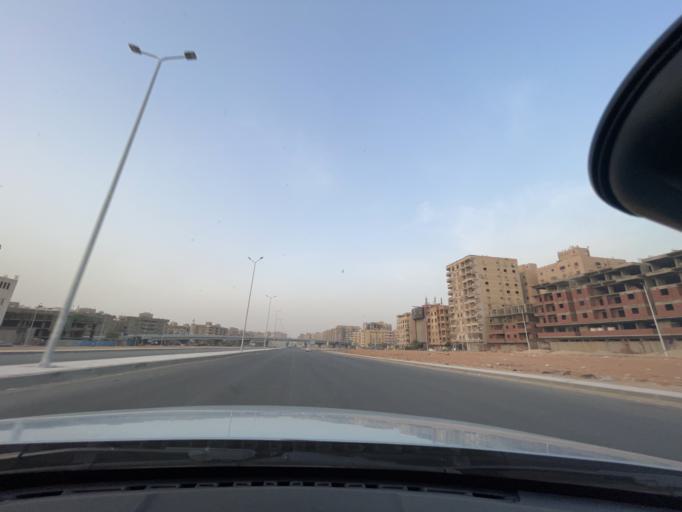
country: EG
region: Muhafazat al Qahirah
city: Cairo
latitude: 30.0555
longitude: 31.3734
